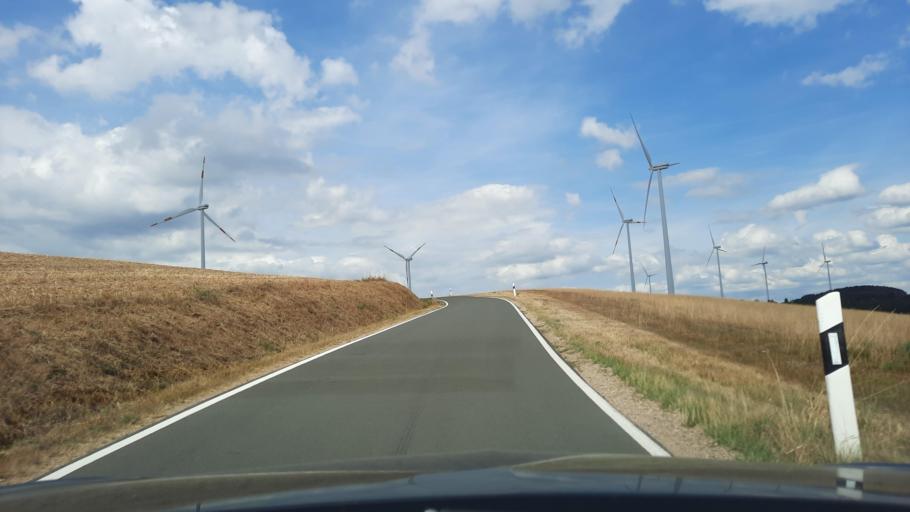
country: DE
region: Rheinland-Pfalz
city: Pronsfeld
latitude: 50.1794
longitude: 6.3282
